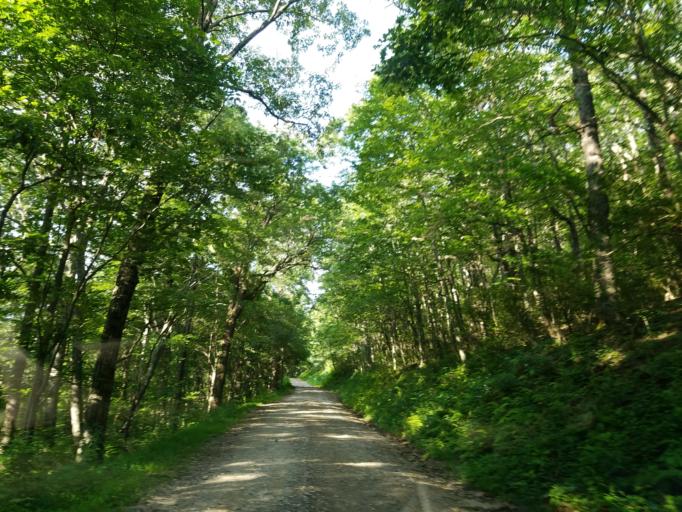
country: US
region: Georgia
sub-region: Lumpkin County
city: Dahlonega
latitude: 34.6652
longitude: -84.1278
